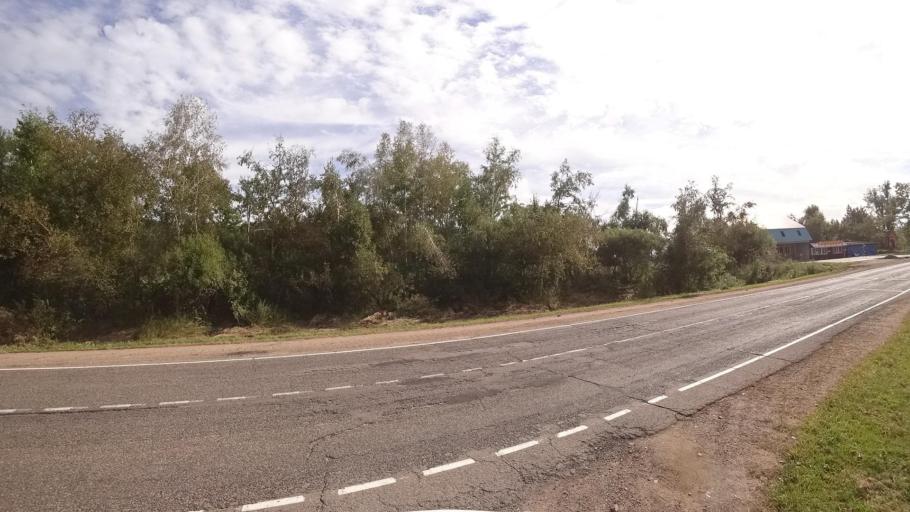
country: RU
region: Primorskiy
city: Dostoyevka
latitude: 44.3224
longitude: 133.4852
